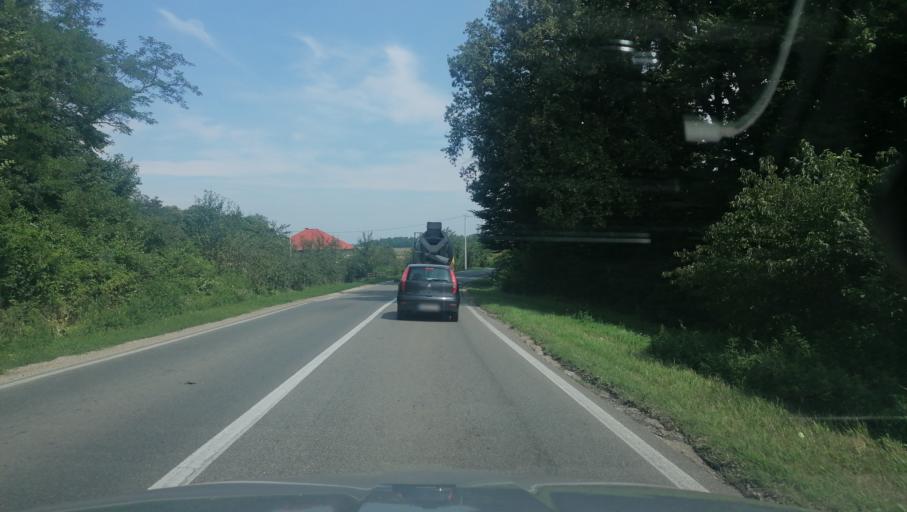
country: BA
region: Republika Srpska
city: Velika Obarska
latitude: 44.7695
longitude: 19.1559
